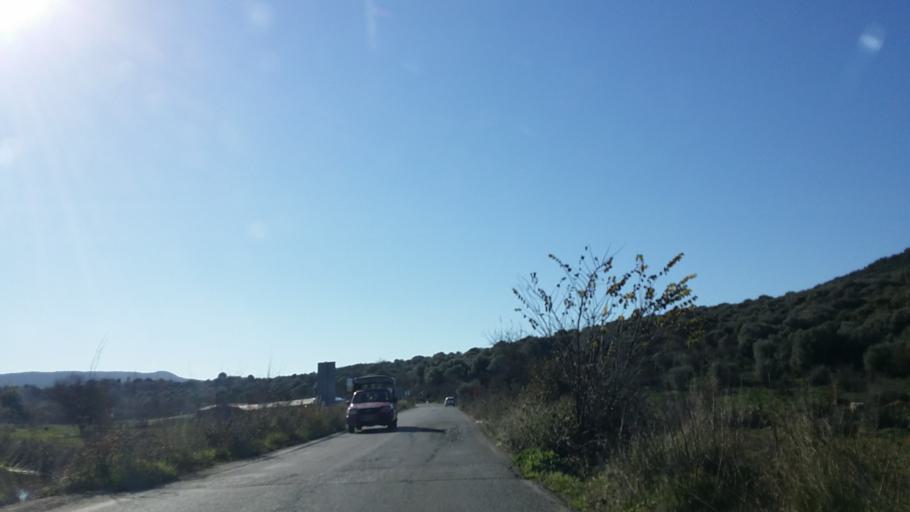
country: GR
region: West Greece
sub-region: Nomos Aitolias kai Akarnanias
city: Vonitsa
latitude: 38.8864
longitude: 20.8976
